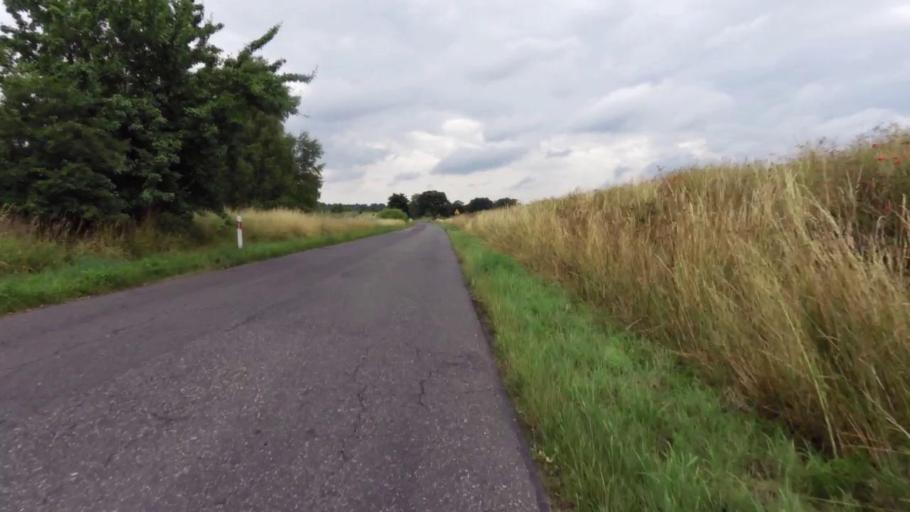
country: PL
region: West Pomeranian Voivodeship
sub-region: Powiat mysliborski
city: Mysliborz
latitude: 52.9592
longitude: 14.8831
